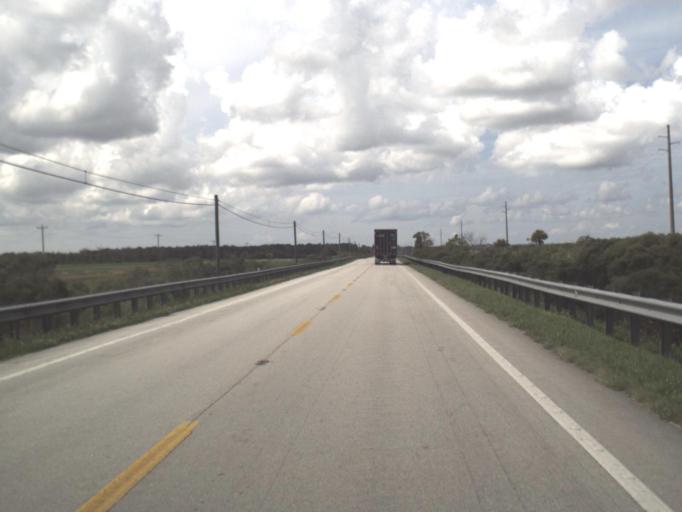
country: US
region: Florida
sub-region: Highlands County
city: Lake Placid
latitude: 27.2085
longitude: -81.2489
